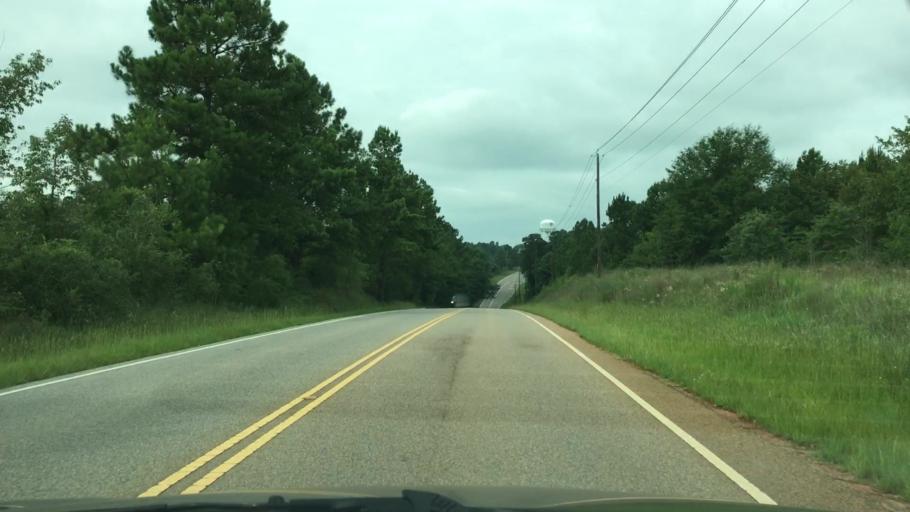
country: US
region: South Carolina
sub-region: Aiken County
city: Belvedere
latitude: 33.5549
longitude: -81.9489
